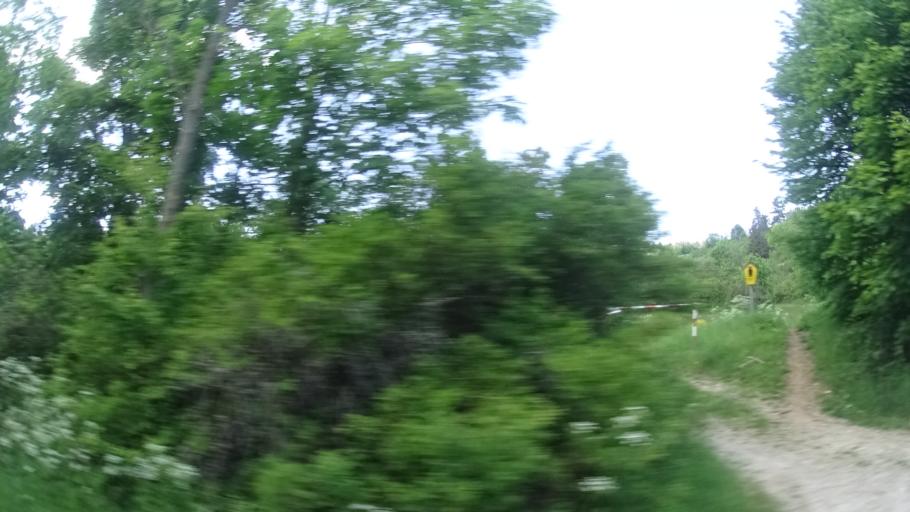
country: DE
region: Thuringia
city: Arnstadt
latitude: 50.8220
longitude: 10.9195
